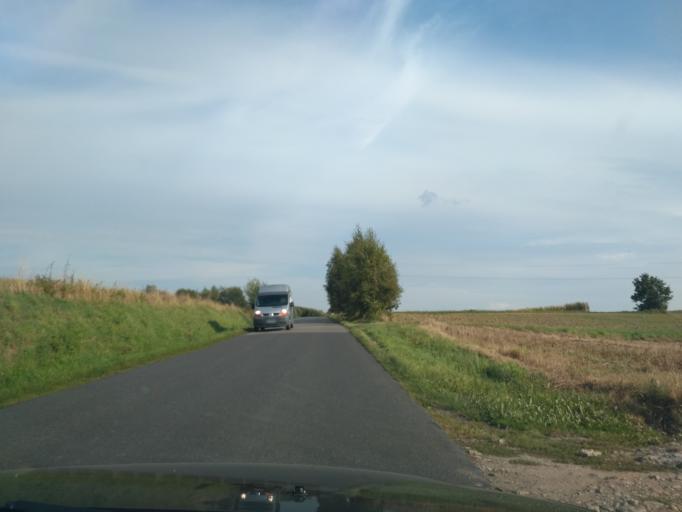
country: PL
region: Subcarpathian Voivodeship
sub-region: Powiat rzeszowski
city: Zglobien
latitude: 50.0067
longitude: 21.8622
